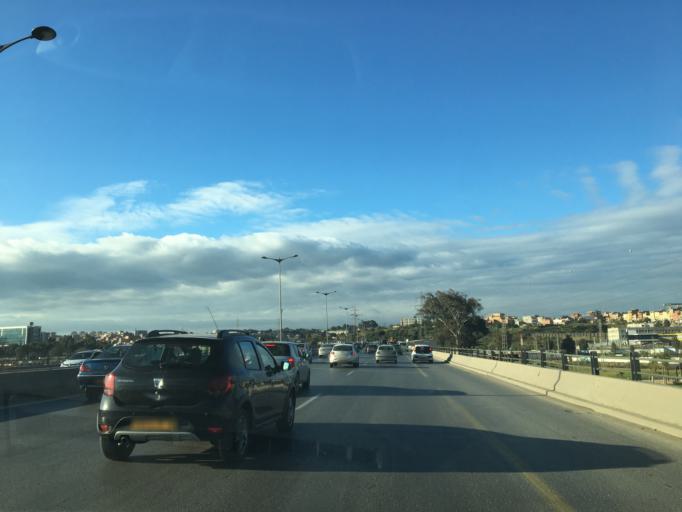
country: DZ
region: Tipaza
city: Baraki
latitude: 36.7040
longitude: 3.1148
